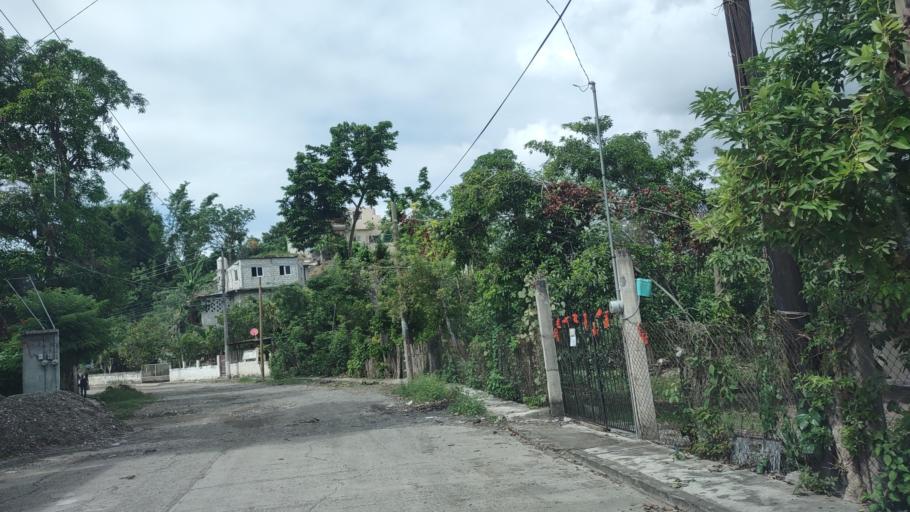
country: MX
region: Veracruz
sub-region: Papantla
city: Residencial Tajin
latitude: 20.5966
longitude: -97.4229
